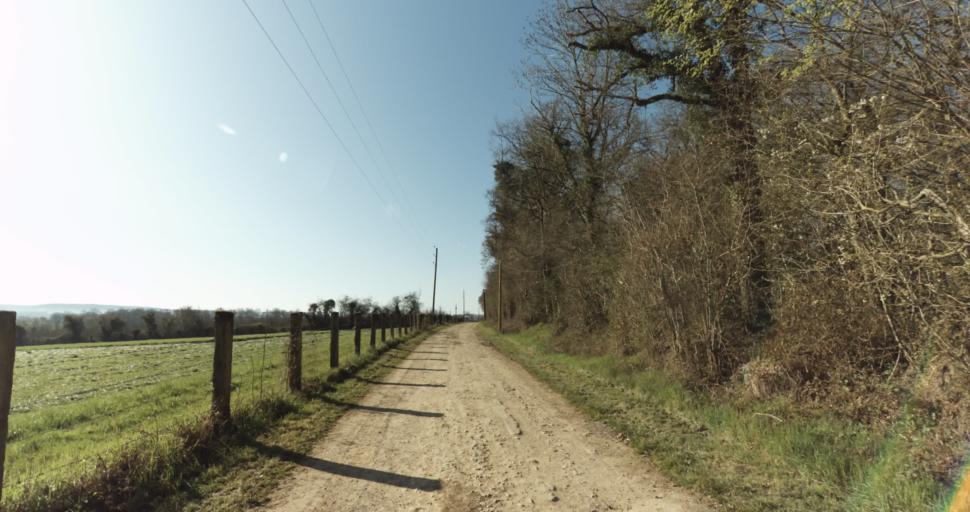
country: FR
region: Lower Normandy
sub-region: Departement du Calvados
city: Saint-Pierre-sur-Dives
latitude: 48.9868
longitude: 0.0004
